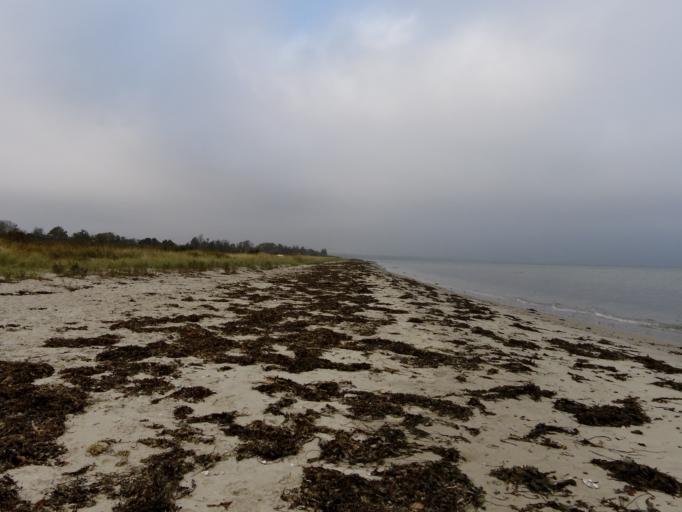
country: DK
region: Central Jutland
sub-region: Arhus Kommune
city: Malling
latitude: 55.9603
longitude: 10.2659
